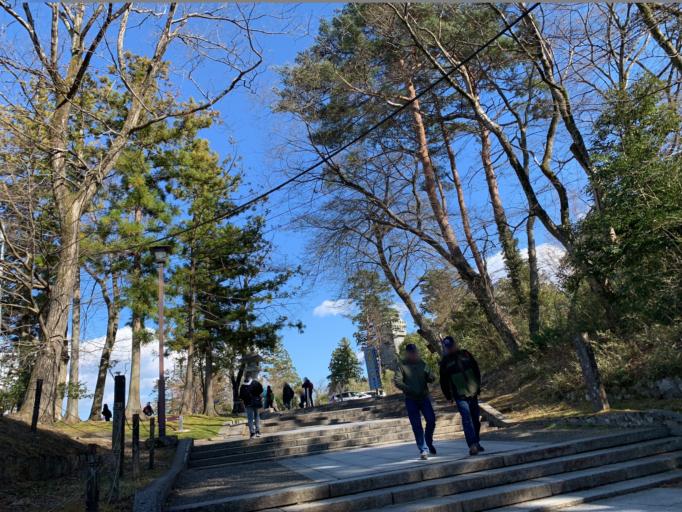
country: JP
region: Miyagi
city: Sendai
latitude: 38.2533
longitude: 140.8556
